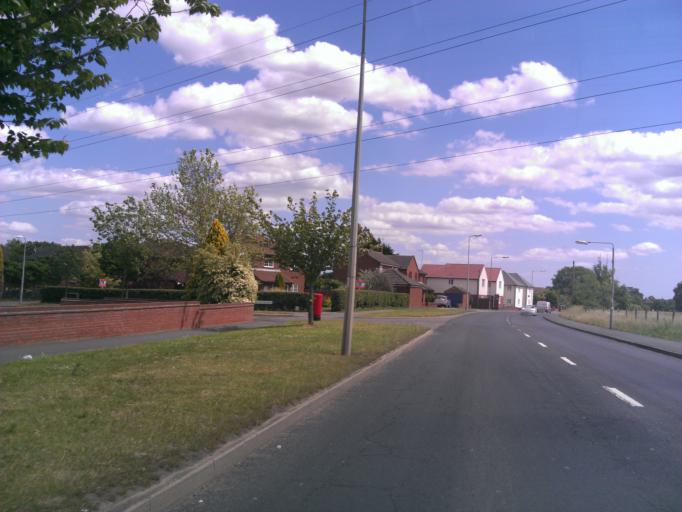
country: GB
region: England
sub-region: Essex
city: Colchester
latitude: 51.8714
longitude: 0.9175
